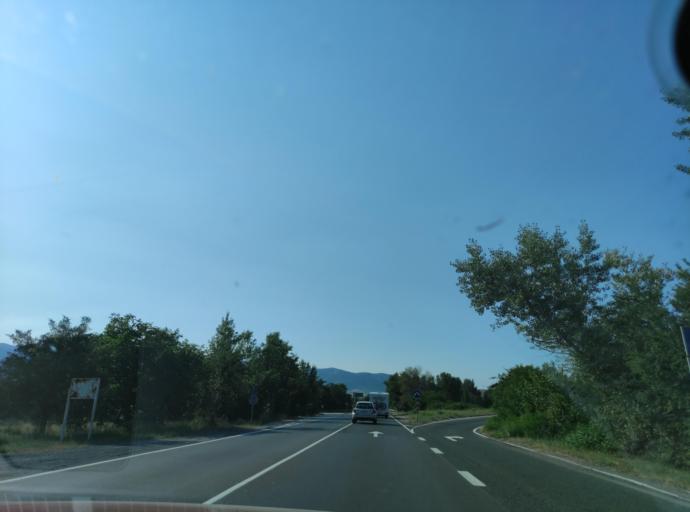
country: BG
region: Blagoevgrad
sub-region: Obshtina Simitli
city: Simitli
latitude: 41.8528
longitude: 23.1373
